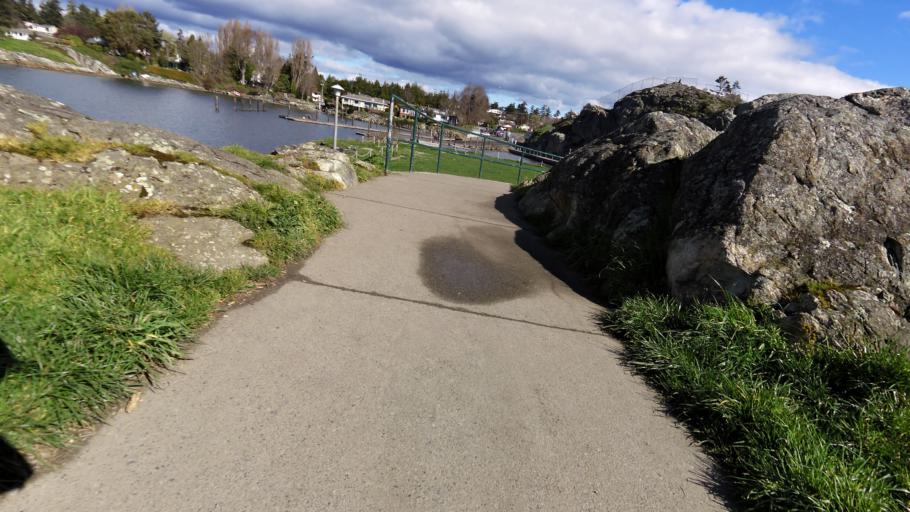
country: CA
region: British Columbia
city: Victoria
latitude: 48.4190
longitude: -123.4114
